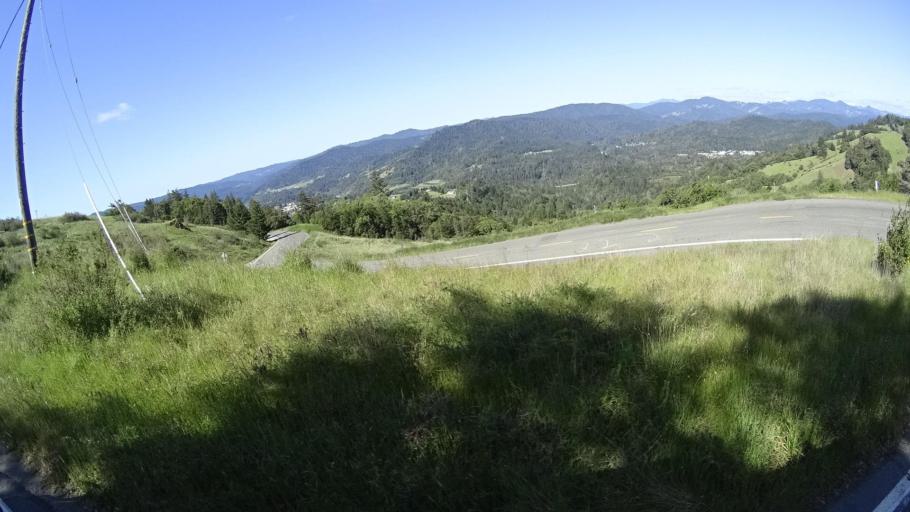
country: US
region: California
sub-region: Humboldt County
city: Redway
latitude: 40.1139
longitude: -123.7734
